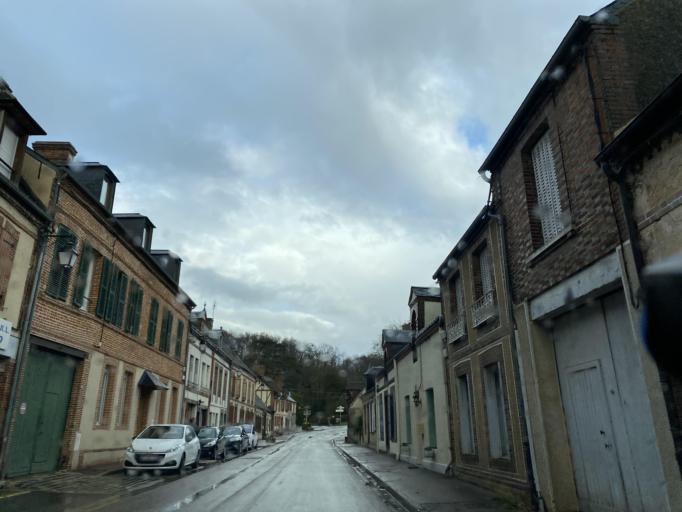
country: FR
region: Haute-Normandie
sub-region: Departement de l'Eure
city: Tillieres-sur-Avre
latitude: 48.7593
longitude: 1.0599
